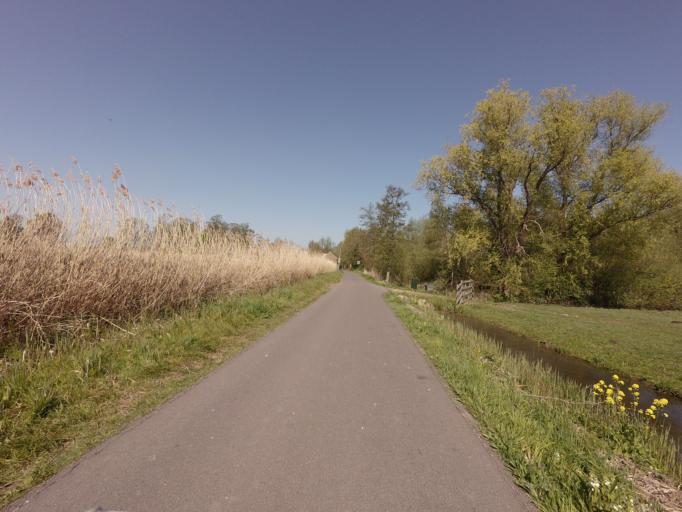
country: NL
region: South Holland
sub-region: Gemeente Gouda
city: Bloemendaal
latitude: 52.0204
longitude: 4.6726
